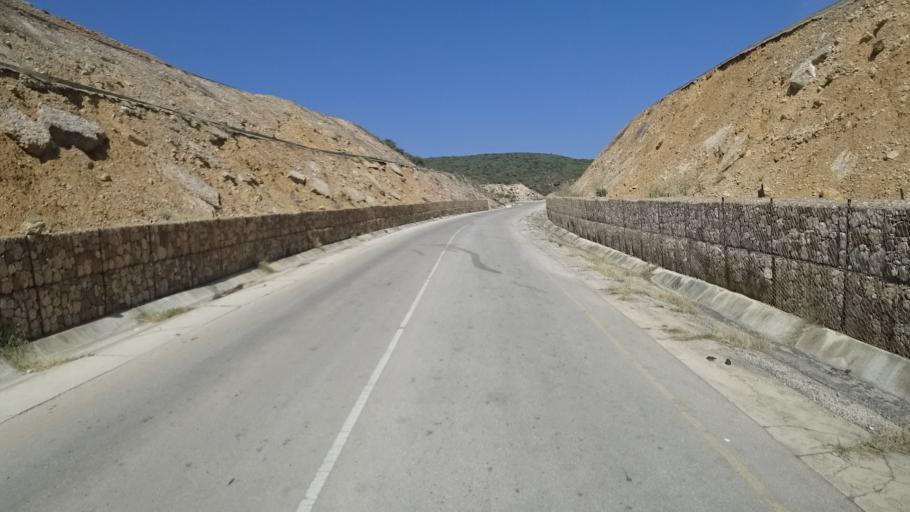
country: OM
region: Zufar
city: Salalah
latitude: 17.0474
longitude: 54.6121
